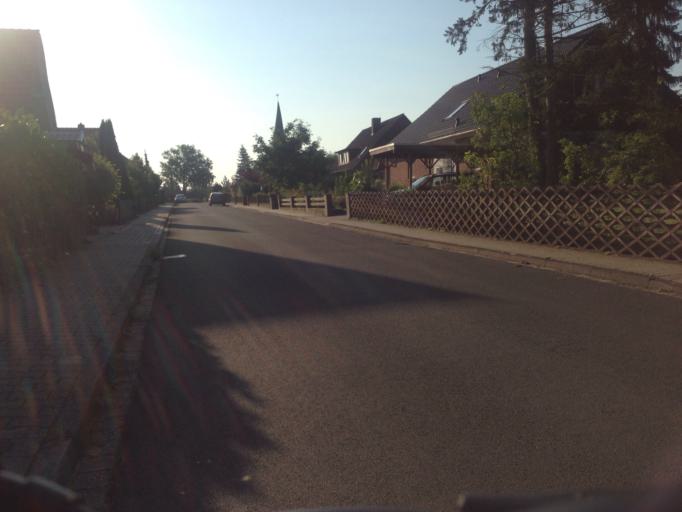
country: DE
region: Lower Saxony
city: Adendorf
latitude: 53.2774
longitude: 10.4366
